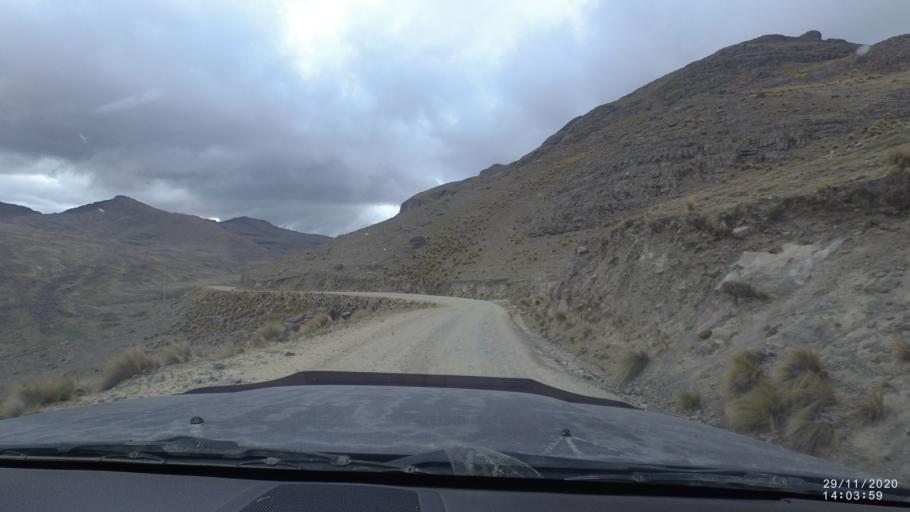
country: BO
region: Cochabamba
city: Sipe Sipe
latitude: -17.1981
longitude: -66.3761
